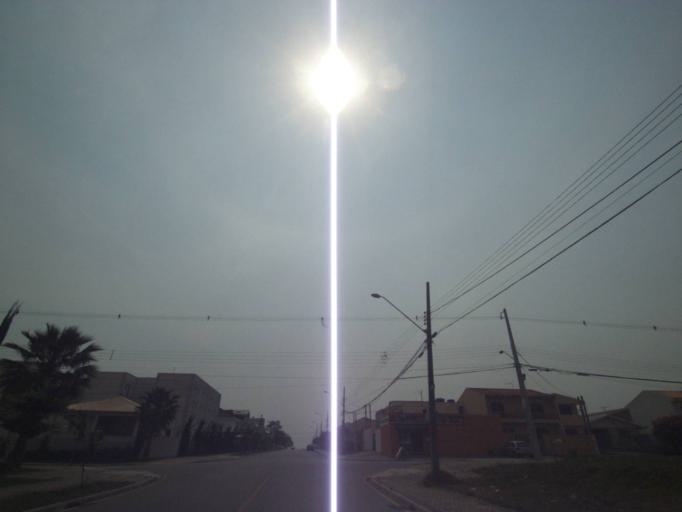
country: BR
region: Parana
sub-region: Sao Jose Dos Pinhais
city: Sao Jose dos Pinhais
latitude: -25.5169
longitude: -49.2831
